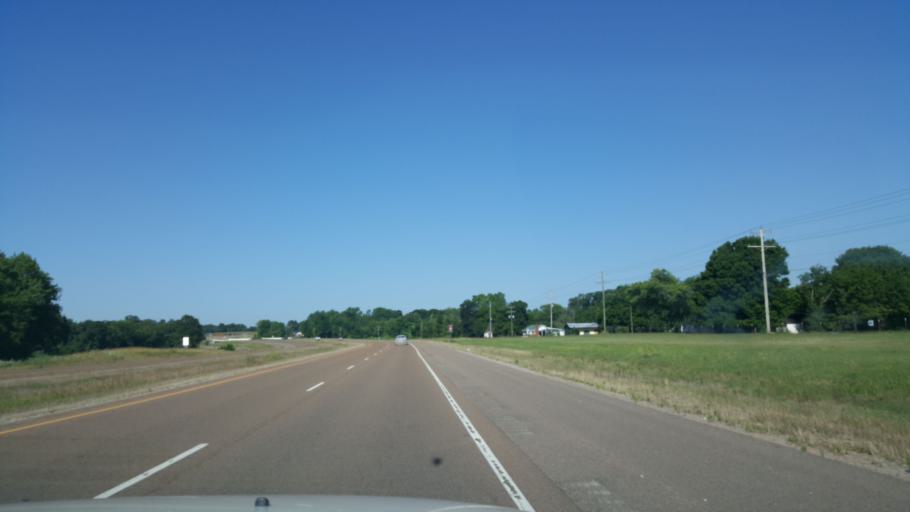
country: US
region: Tennessee
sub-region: Hardin County
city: Olivet
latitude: 35.2319
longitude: -88.1878
